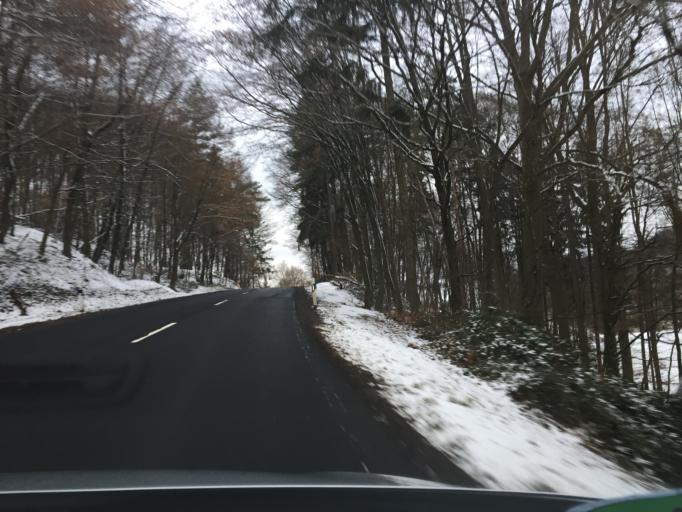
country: DE
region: Bavaria
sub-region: Regierungsbezirk Unterfranken
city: Krombach
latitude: 50.1039
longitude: 9.2238
